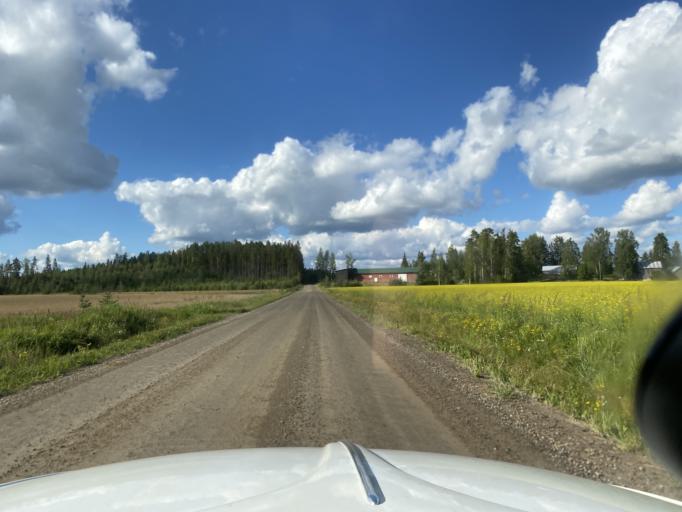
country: FI
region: Pirkanmaa
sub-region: Lounais-Pirkanmaa
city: Punkalaidun
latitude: 61.1133
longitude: 23.2741
